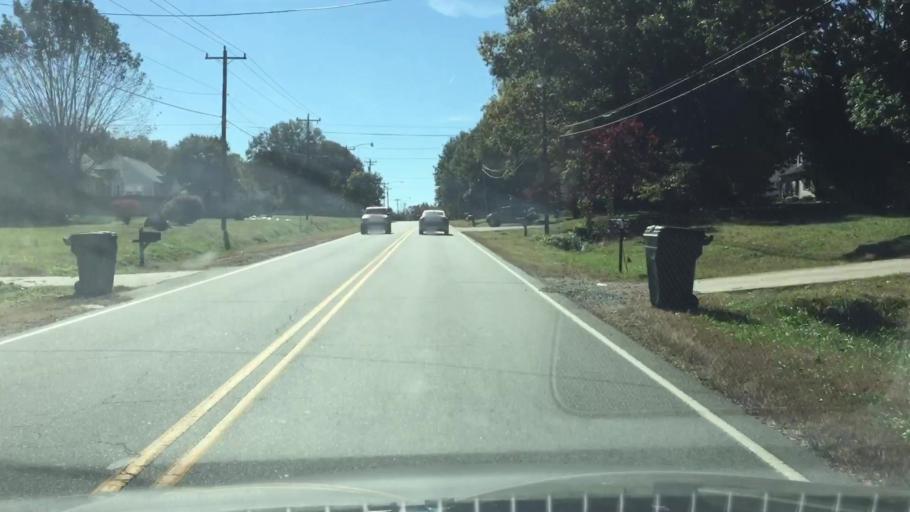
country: US
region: North Carolina
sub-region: Rockingham County
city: Reidsville
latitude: 36.3270
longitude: -79.6657
